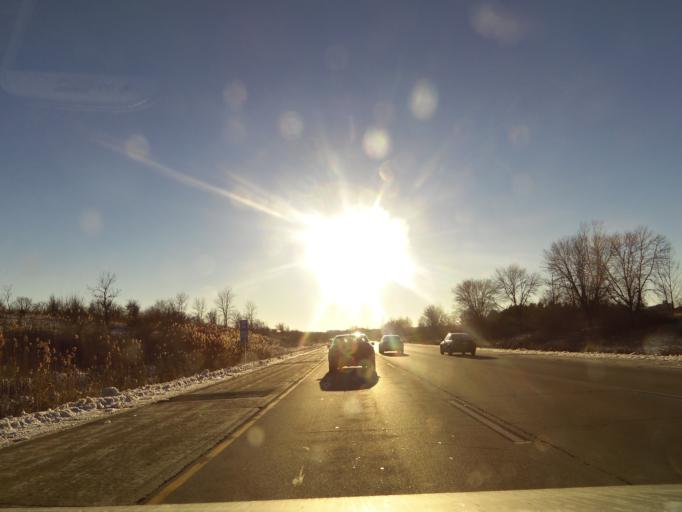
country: US
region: Wisconsin
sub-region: Racine County
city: Caledonia
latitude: 42.8512
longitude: -87.9432
